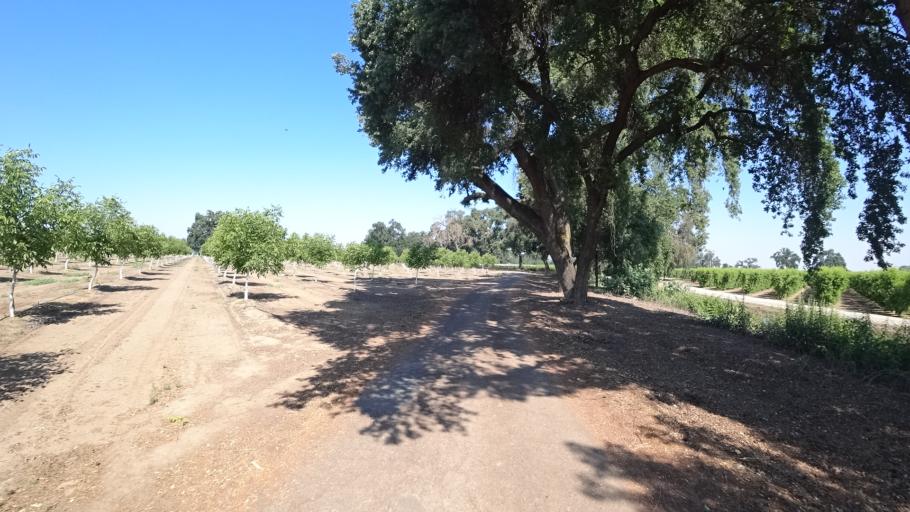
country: US
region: California
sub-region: Fresno County
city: Kingsburg
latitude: 36.4412
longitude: -119.5667
